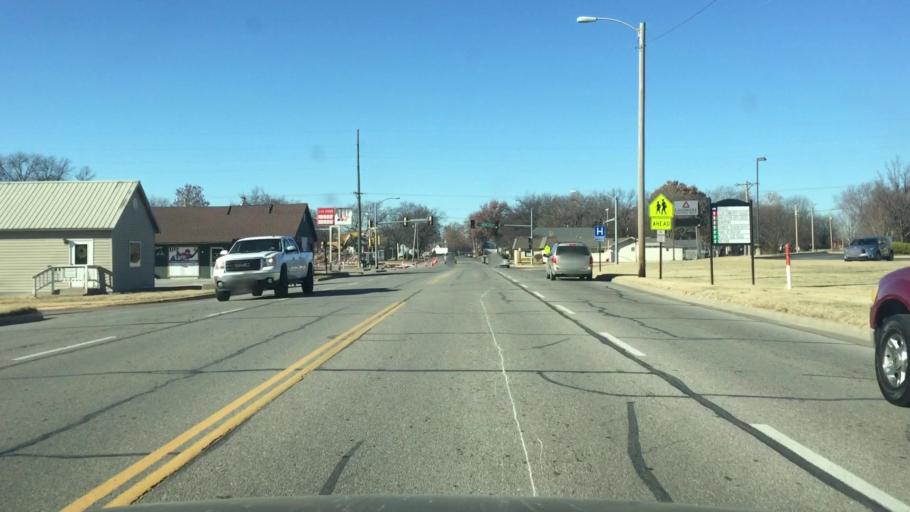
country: US
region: Kansas
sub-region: Allen County
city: Iola
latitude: 37.9222
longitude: -95.3894
